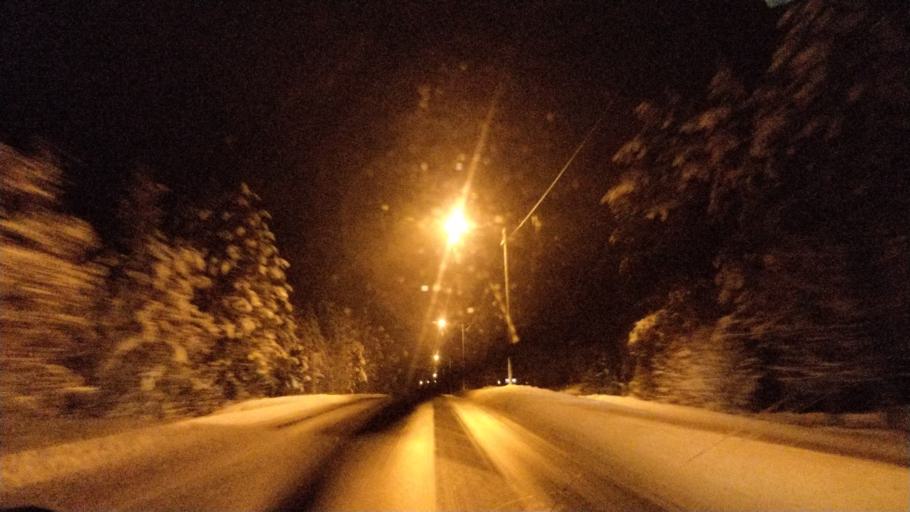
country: FI
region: Lapland
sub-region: Rovaniemi
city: Rovaniemi
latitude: 66.3205
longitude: 25.3586
